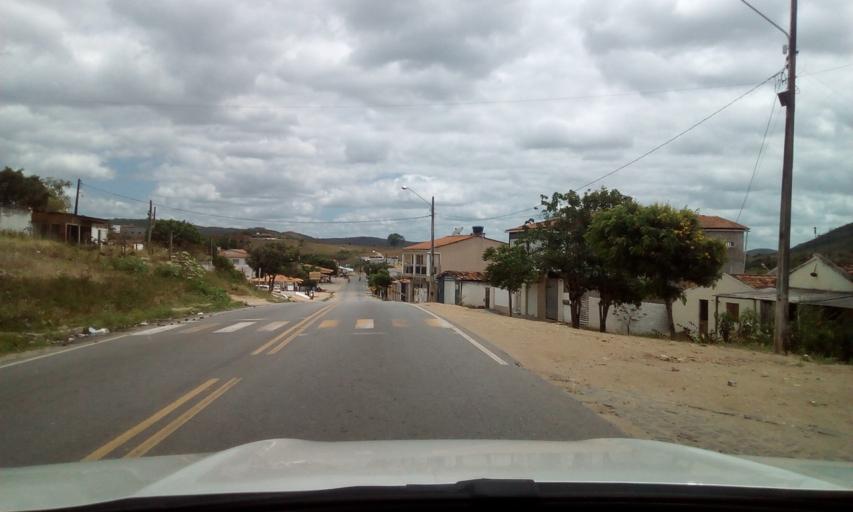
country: BR
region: Paraiba
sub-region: Serra Redonda
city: Alagoa Grande
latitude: -7.1730
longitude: -35.5909
